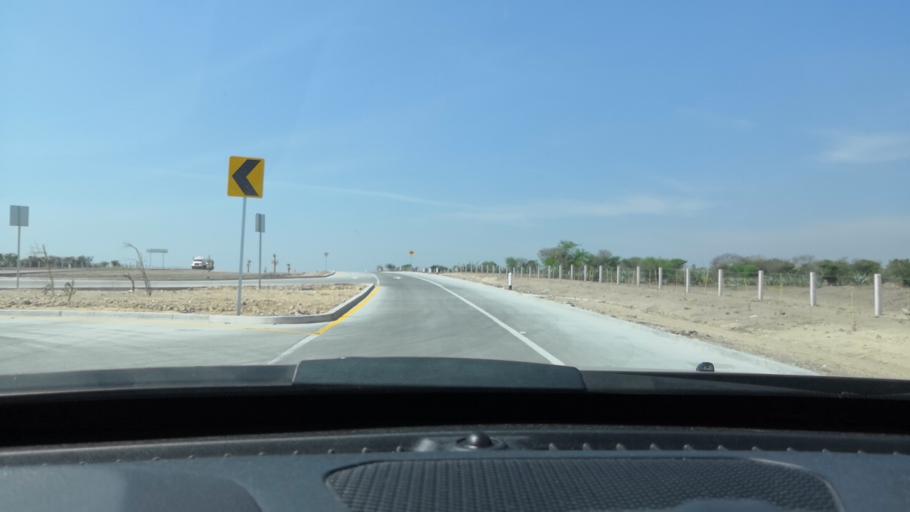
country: MX
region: Guanajuato
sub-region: Leon
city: Centro Familiar la Soledad
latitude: 21.0945
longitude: -101.7887
